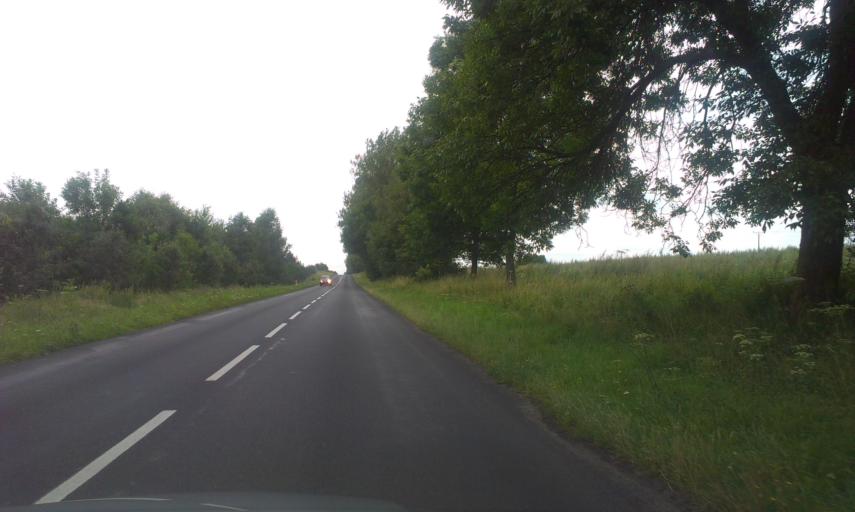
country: PL
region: West Pomeranian Voivodeship
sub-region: Powiat swidwinski
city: Polczyn-Zdroj
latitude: 53.8605
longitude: 16.0703
